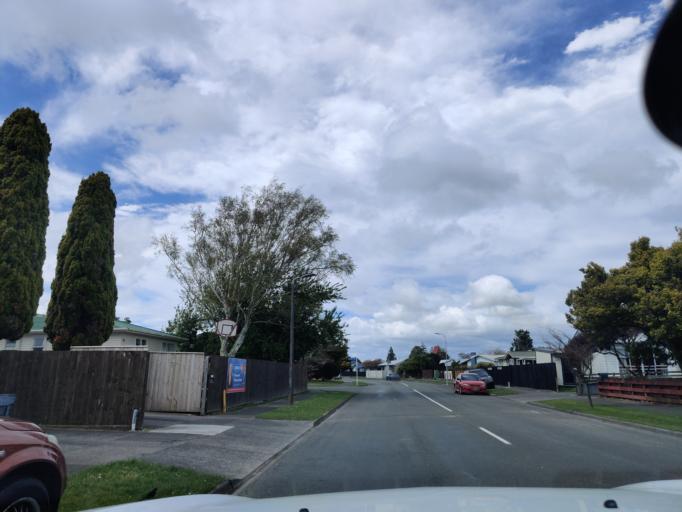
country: NZ
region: Manawatu-Wanganui
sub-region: Palmerston North City
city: Palmerston North
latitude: -40.3604
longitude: 175.5833
